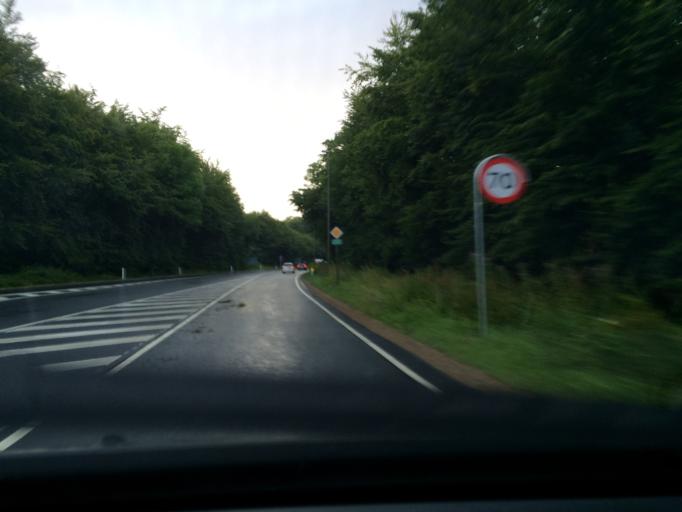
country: DK
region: Zealand
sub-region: Guldborgsund Kommune
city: Nykobing Falster
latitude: 54.7908
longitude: 11.8730
